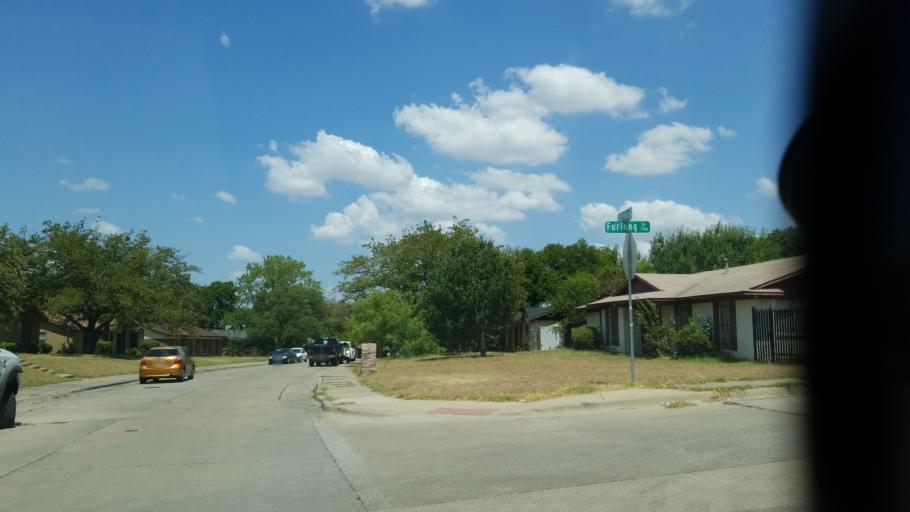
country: US
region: Texas
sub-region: Dallas County
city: Cockrell Hill
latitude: 32.7384
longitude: -96.9221
